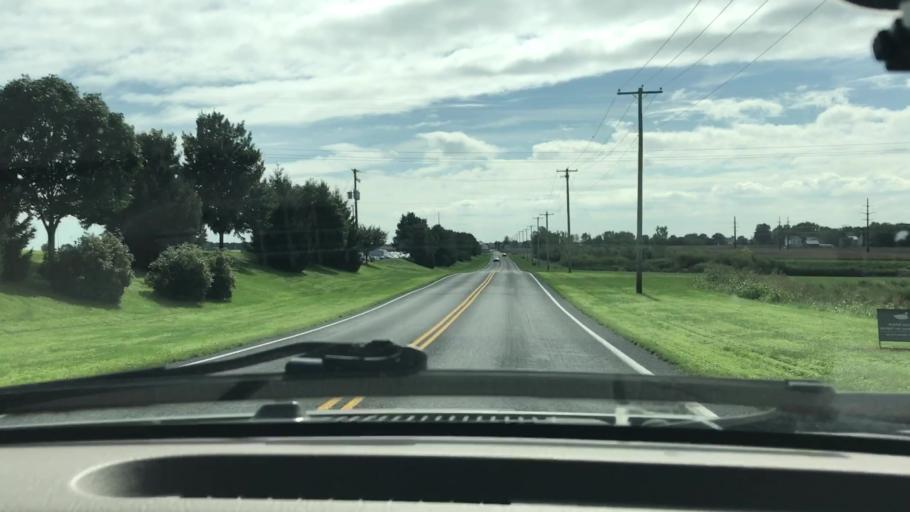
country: US
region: Pennsylvania
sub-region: Lancaster County
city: Manheim
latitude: 40.1382
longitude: -76.4046
